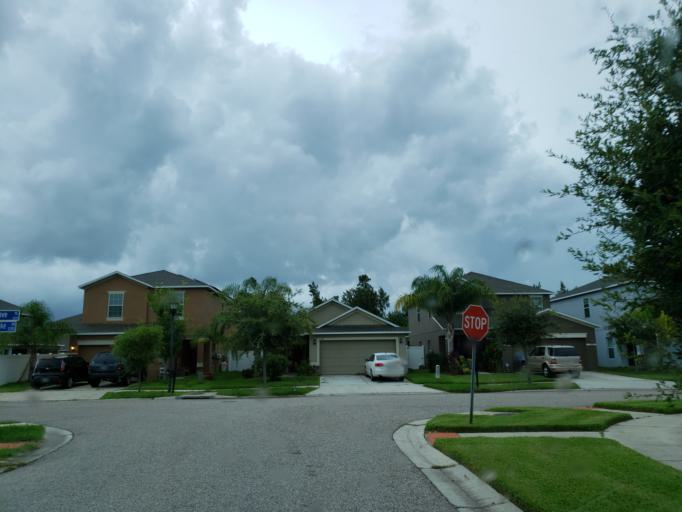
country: US
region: Florida
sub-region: Hillsborough County
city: Ruskin
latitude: 27.7290
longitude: -82.4043
